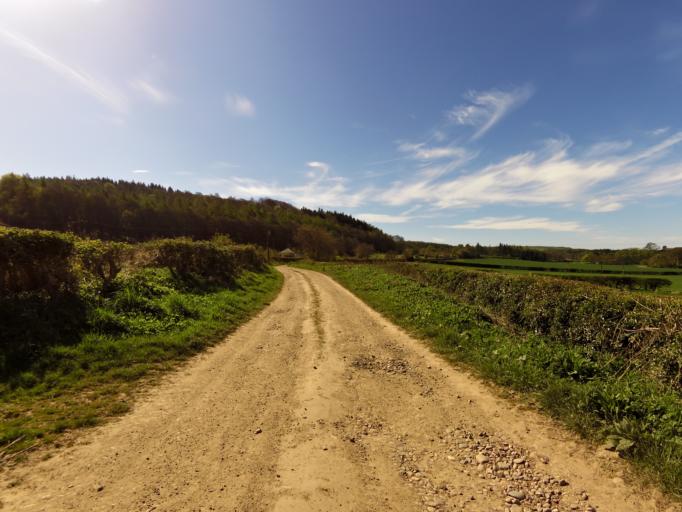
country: GB
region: Scotland
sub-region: Fife
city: Cupar
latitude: 56.3989
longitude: -3.0651
